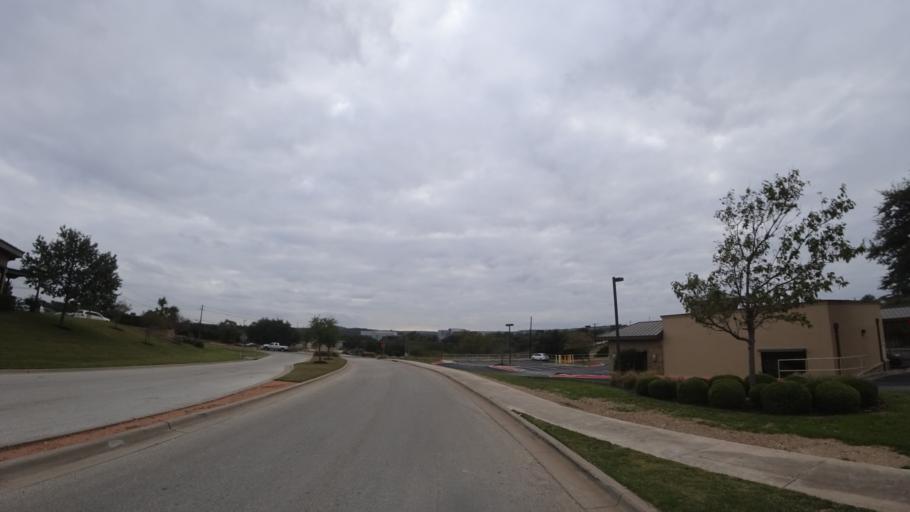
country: US
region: Texas
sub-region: Travis County
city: Bee Cave
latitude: 30.3116
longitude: -97.9132
